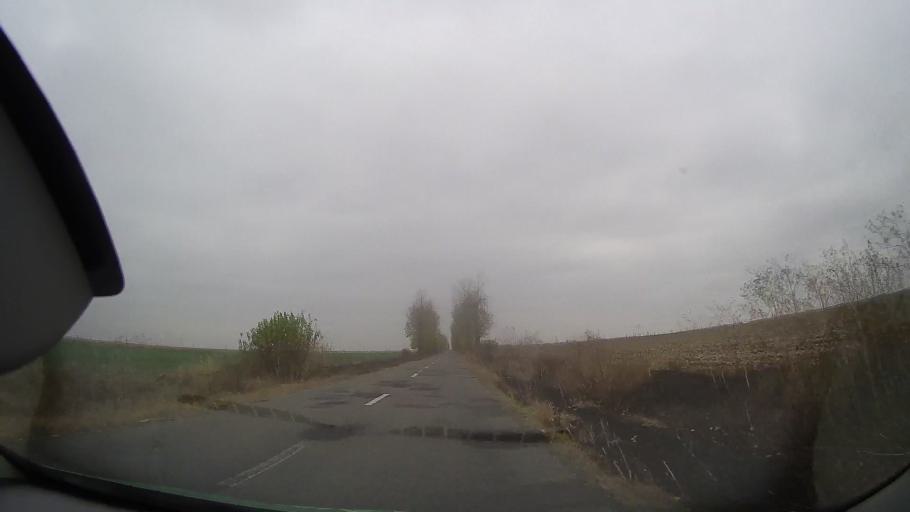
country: RO
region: Ialomita
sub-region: Comuna Grindu
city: Grindu
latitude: 44.7552
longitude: 26.8739
